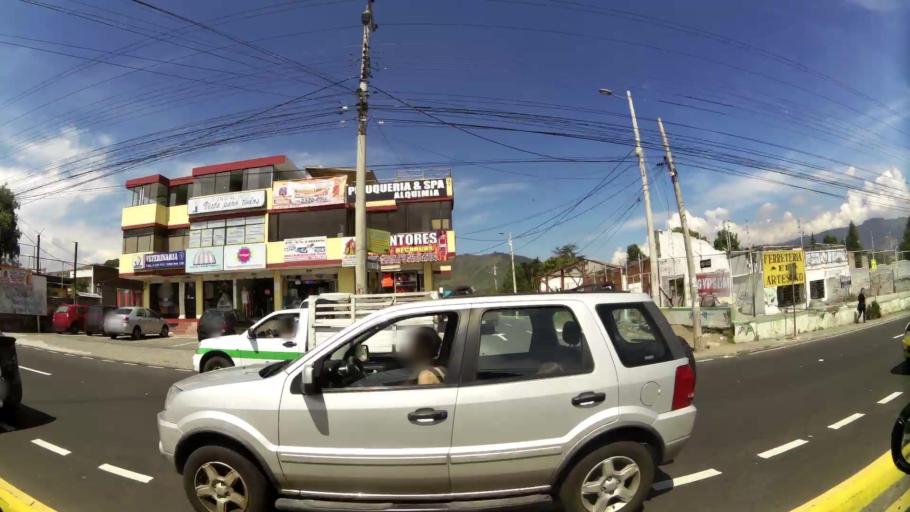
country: EC
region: Pichincha
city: Quito
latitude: -0.2144
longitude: -78.4074
